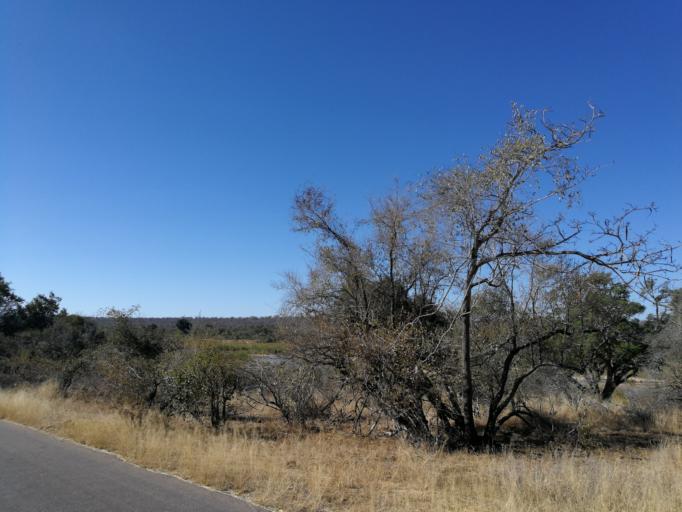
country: ZA
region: Mpumalanga
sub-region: Ehlanzeni District
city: Komatipoort
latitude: -24.9914
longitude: 31.7670
